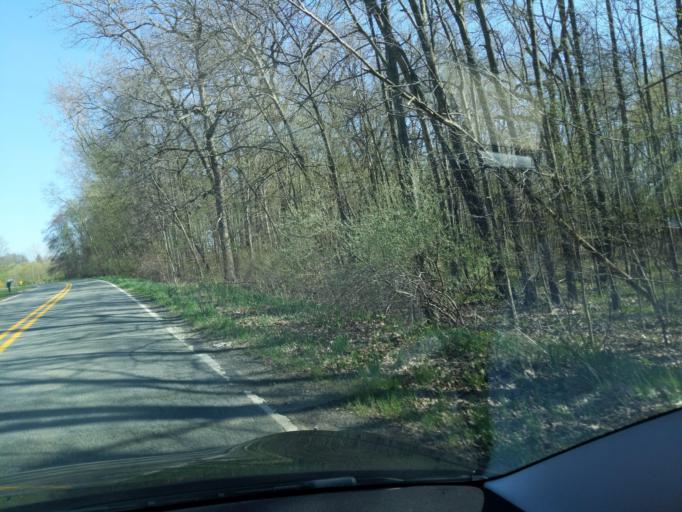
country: US
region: Michigan
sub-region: Ingham County
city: Stockbridge
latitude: 42.4445
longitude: -84.1009
